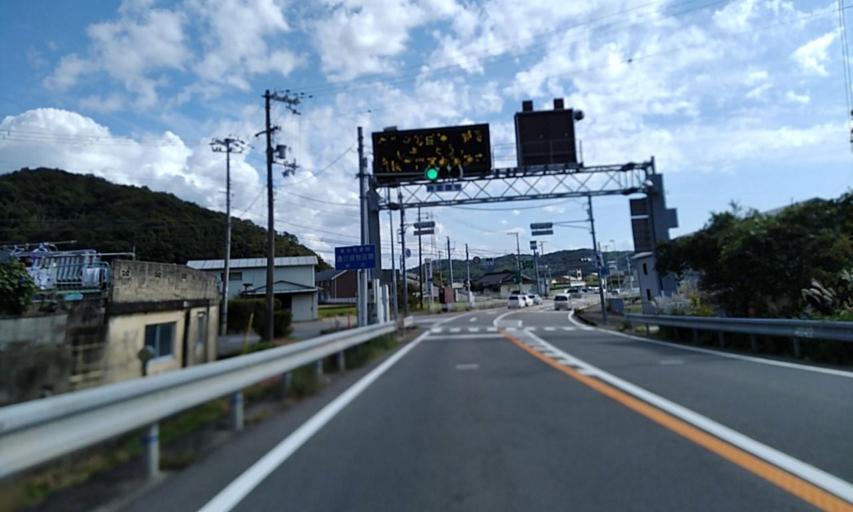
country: JP
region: Wakayama
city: Gobo
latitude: 33.9326
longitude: 135.1409
